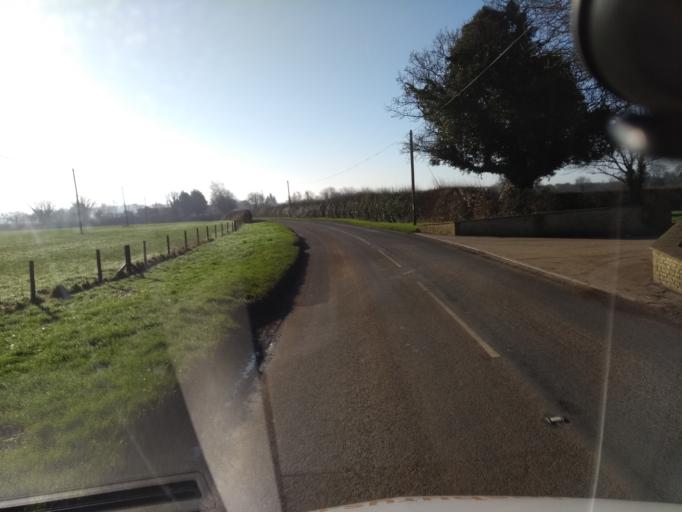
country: GB
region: England
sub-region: Somerset
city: Wincanton
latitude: 51.0757
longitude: -2.4123
